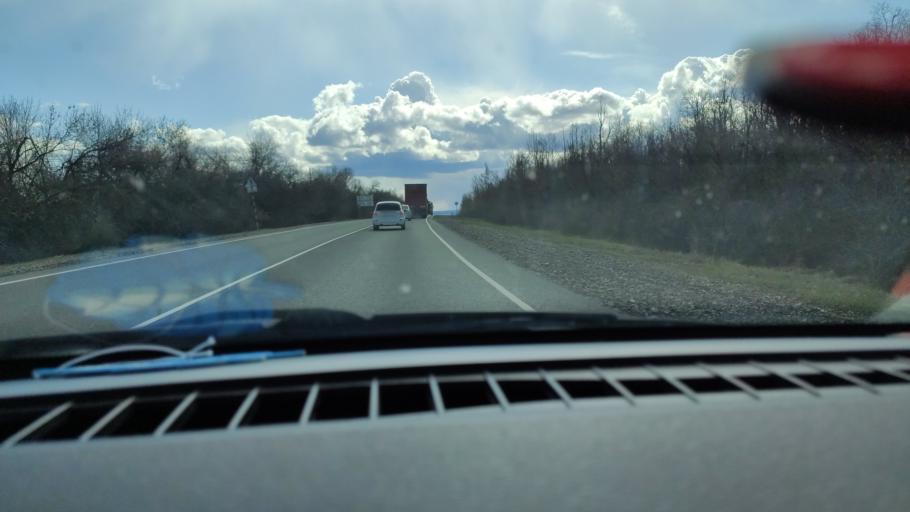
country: RU
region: Saratov
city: Dukhovnitskoye
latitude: 52.6224
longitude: 48.1751
